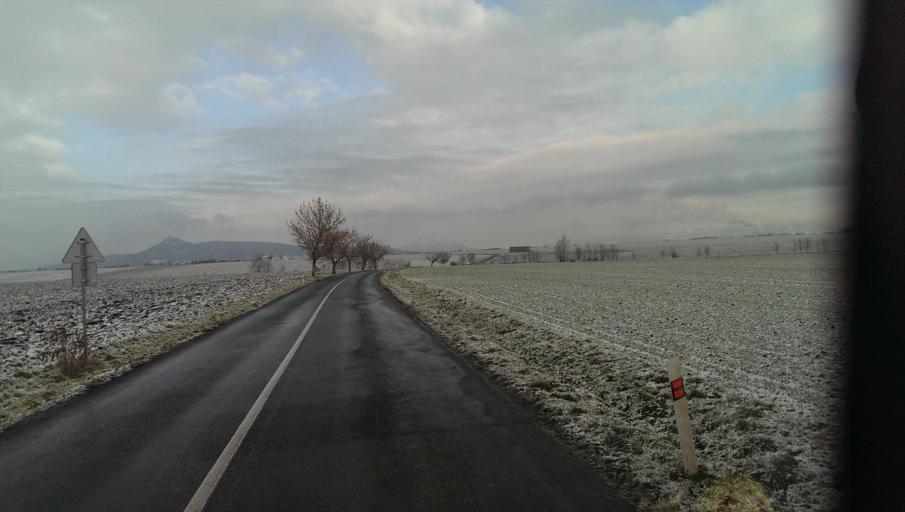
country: CZ
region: Ustecky
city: Trebenice
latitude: 50.4485
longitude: 13.9984
